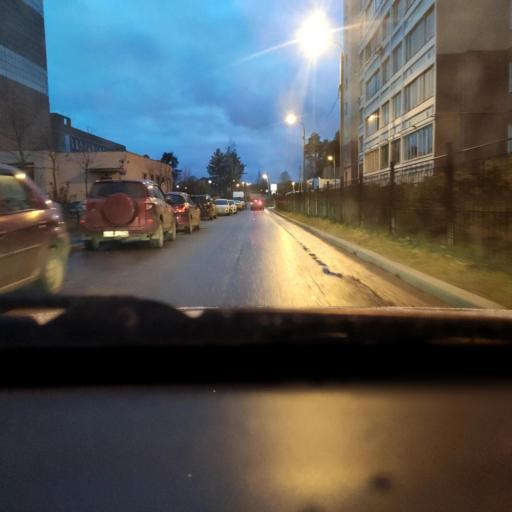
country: RU
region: Perm
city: Kondratovo
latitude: 58.0386
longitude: 56.1219
